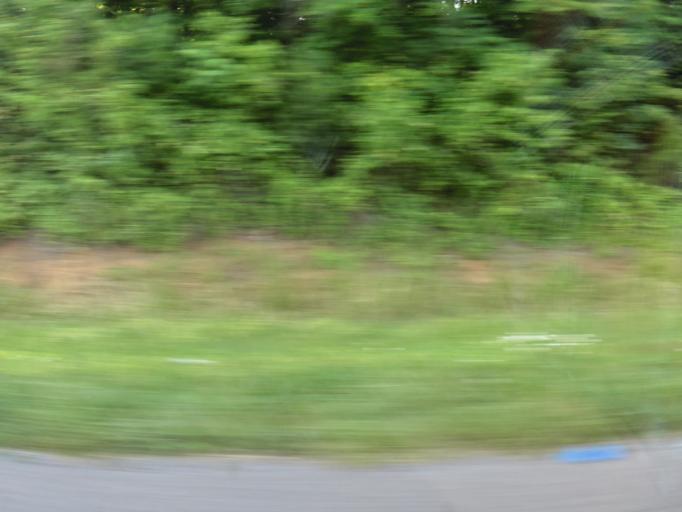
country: US
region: Tennessee
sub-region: Knox County
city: Knoxville
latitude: 35.8957
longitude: -83.8846
